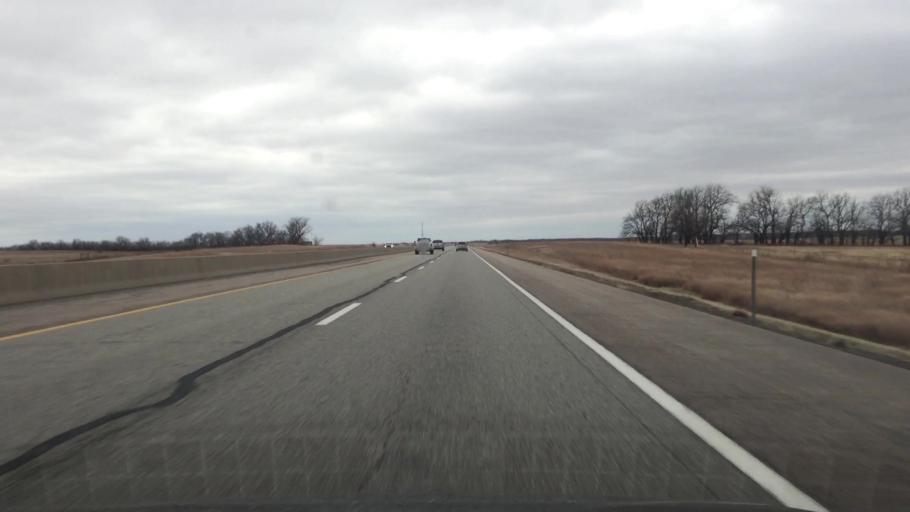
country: US
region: Kansas
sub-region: Butler County
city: El Dorado
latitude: 37.9816
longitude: -96.7108
